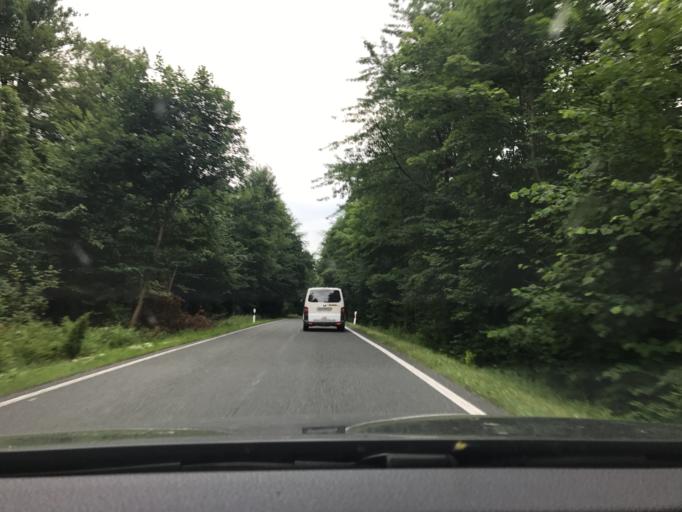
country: DE
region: Thuringia
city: Helmsdorf
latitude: 51.2801
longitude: 10.3601
